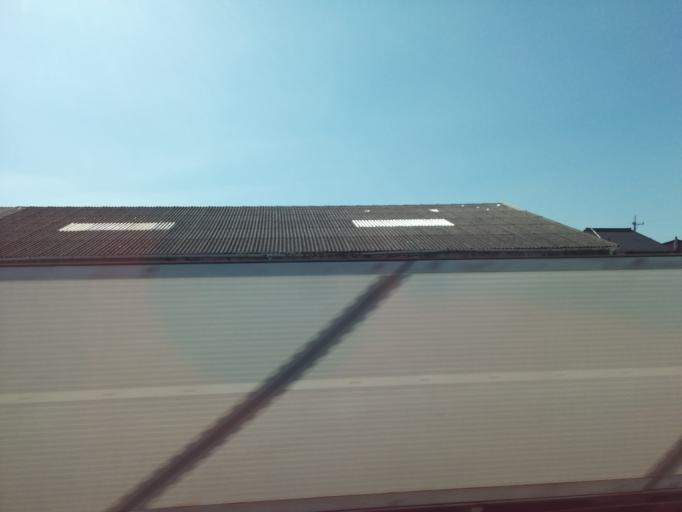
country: JP
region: Aichi
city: Toyohashi
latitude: 34.7276
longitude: 137.4301
